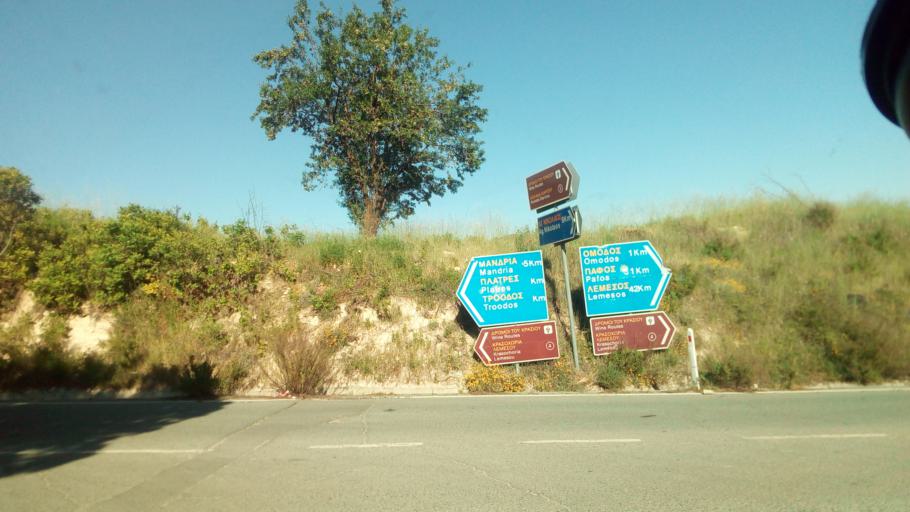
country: CY
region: Limassol
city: Pachna
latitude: 34.8551
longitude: 32.8063
